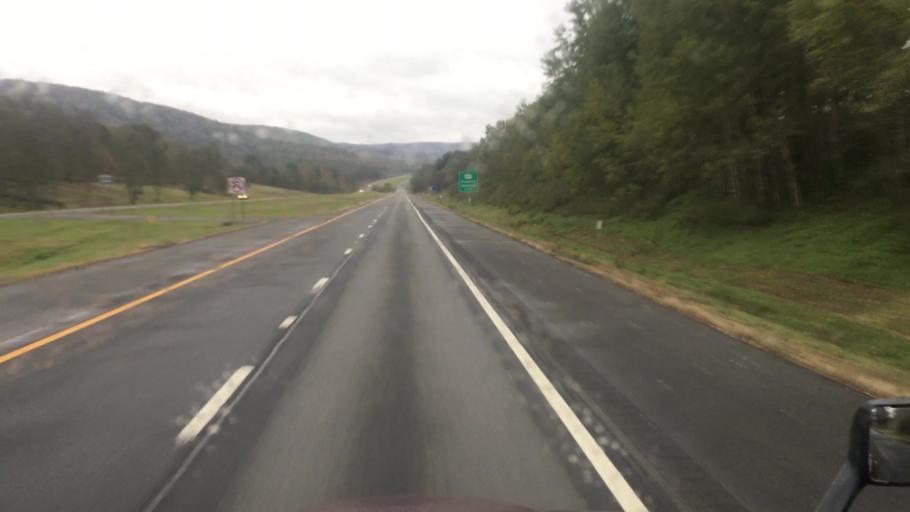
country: US
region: New York
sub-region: Otsego County
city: Unadilla
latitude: 42.3493
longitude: -75.2641
